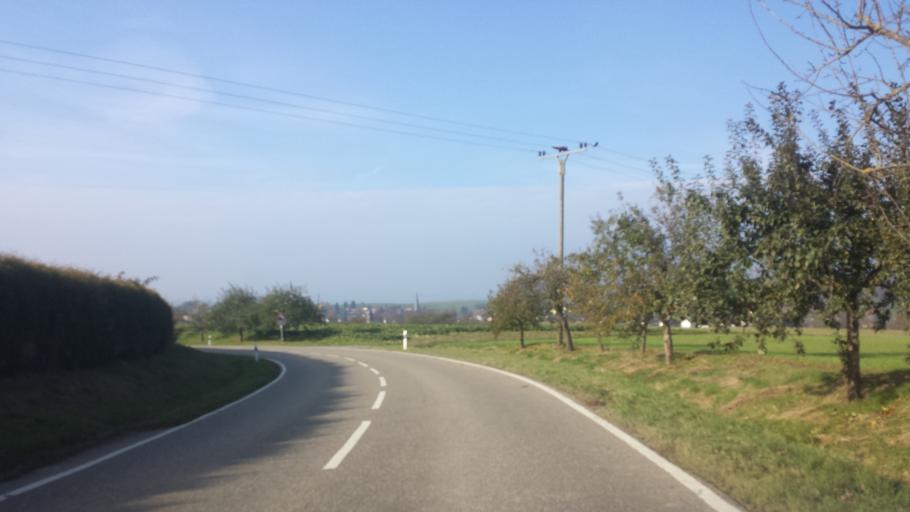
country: DE
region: Baden-Wuerttemberg
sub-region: Karlsruhe Region
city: Epfenbach
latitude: 49.3349
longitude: 8.9218
